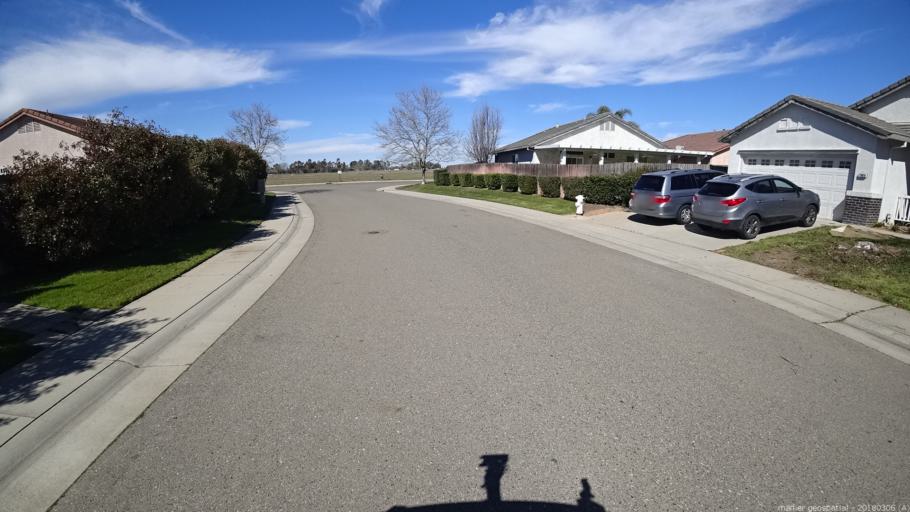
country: US
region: California
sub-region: Sacramento County
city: Vineyard
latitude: 38.4701
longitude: -121.3597
